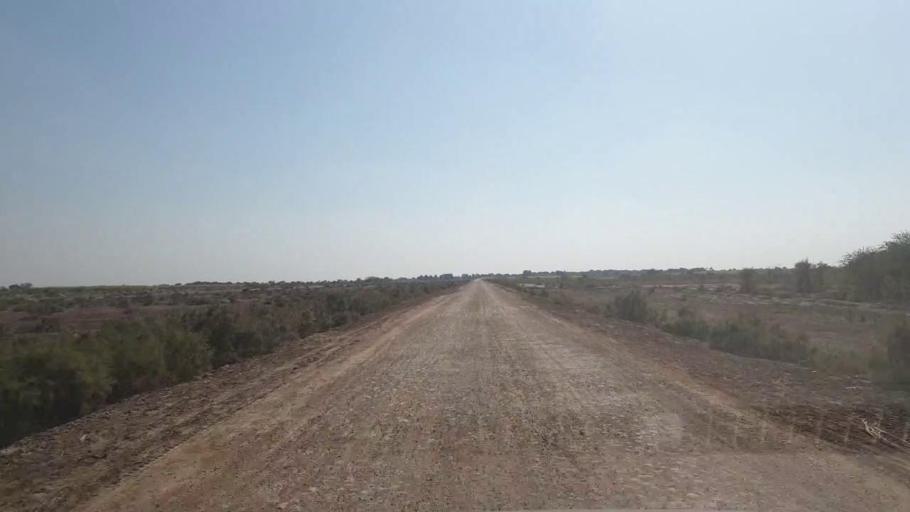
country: PK
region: Sindh
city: Chambar
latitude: 25.3262
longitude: 68.7399
